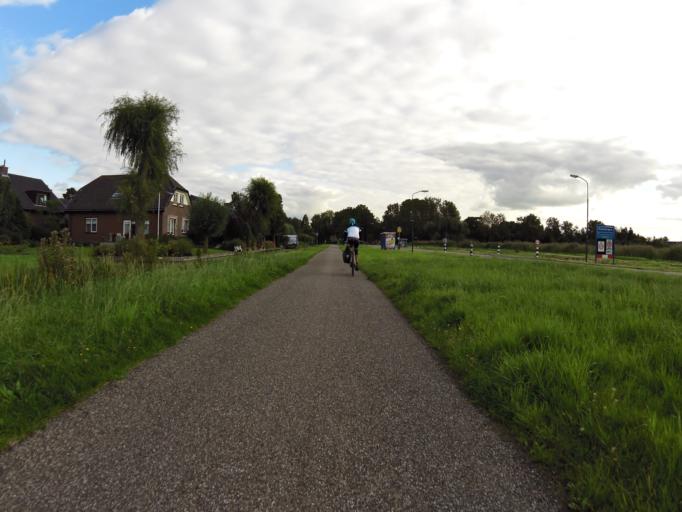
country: NL
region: Utrecht
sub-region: Stichtse Vecht
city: Breukelen
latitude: 52.1526
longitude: 4.9472
